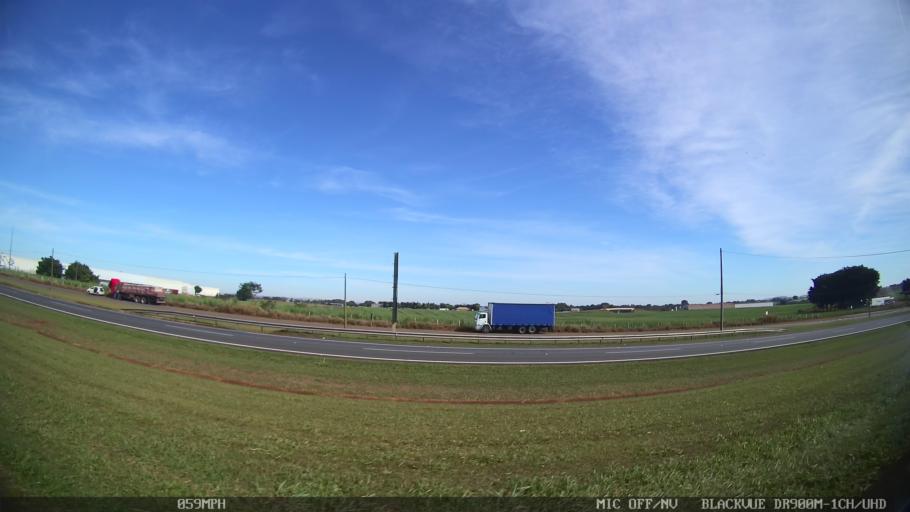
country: BR
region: Sao Paulo
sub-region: Cordeiropolis
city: Cordeiropolis
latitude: -22.4886
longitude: -47.3993
